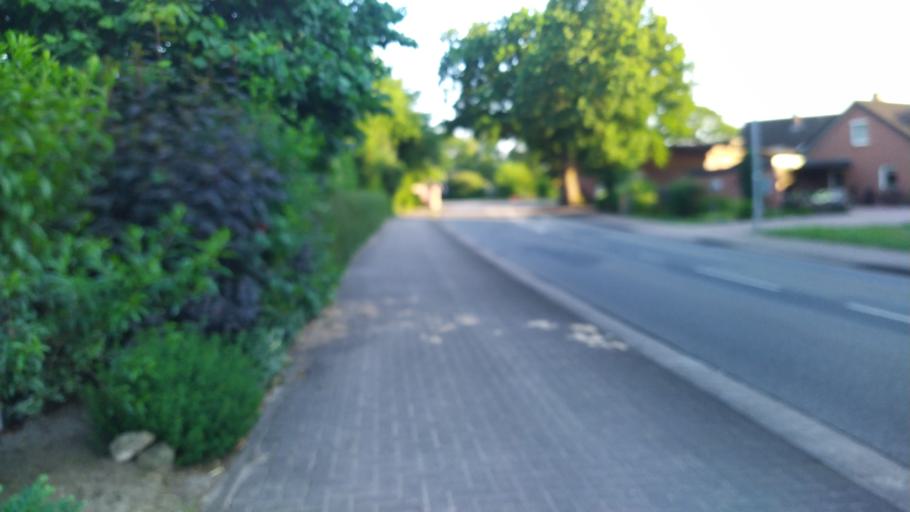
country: DE
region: Lower Saxony
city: Ebersdorf
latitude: 53.5274
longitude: 9.0523
